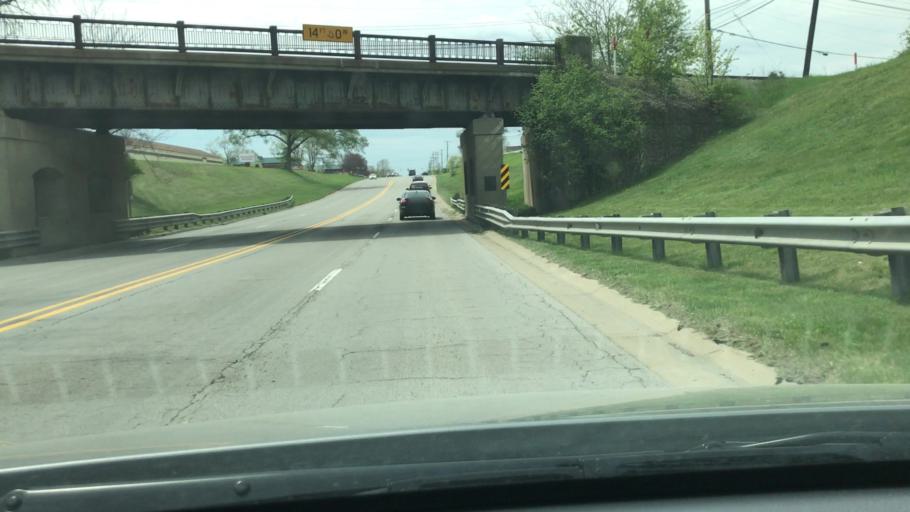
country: US
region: Michigan
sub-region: Wayne County
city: Plymouth
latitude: 42.3592
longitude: -83.4535
